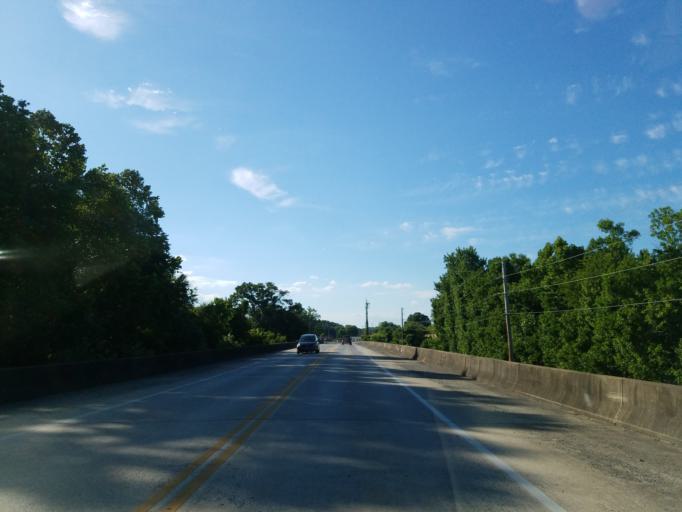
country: US
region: Georgia
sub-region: Gordon County
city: Calhoun
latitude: 34.5760
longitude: -84.9410
